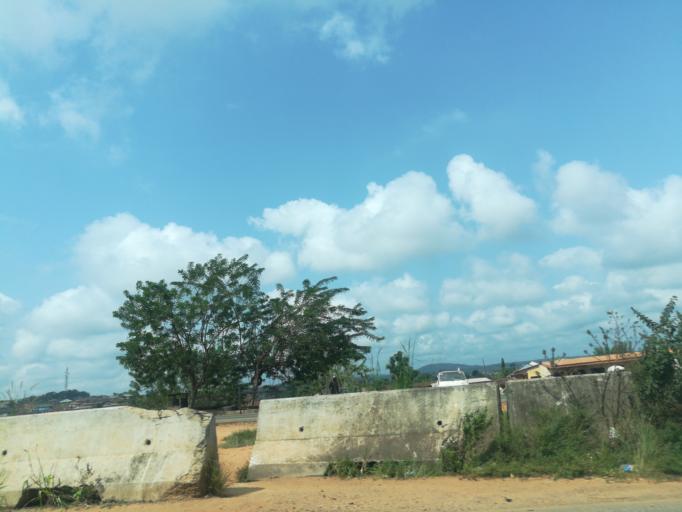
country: NG
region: Oyo
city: Moniya
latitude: 7.5321
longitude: 3.9167
